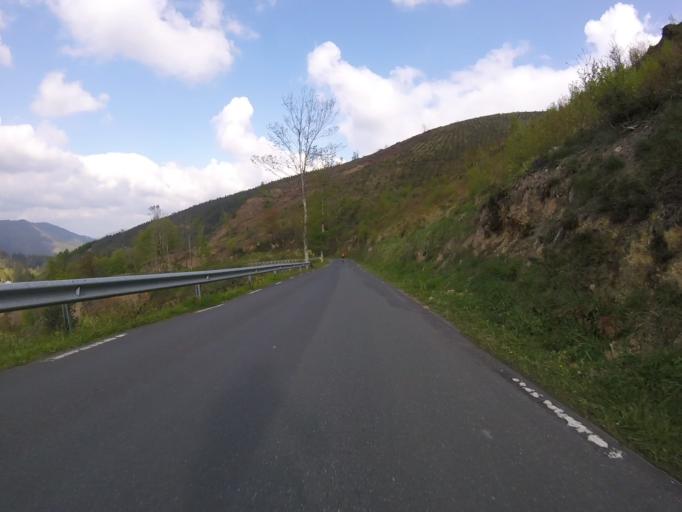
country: ES
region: Basque Country
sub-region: Provincia de Guipuzcoa
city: Azkoitia
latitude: 43.2053
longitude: -2.3547
